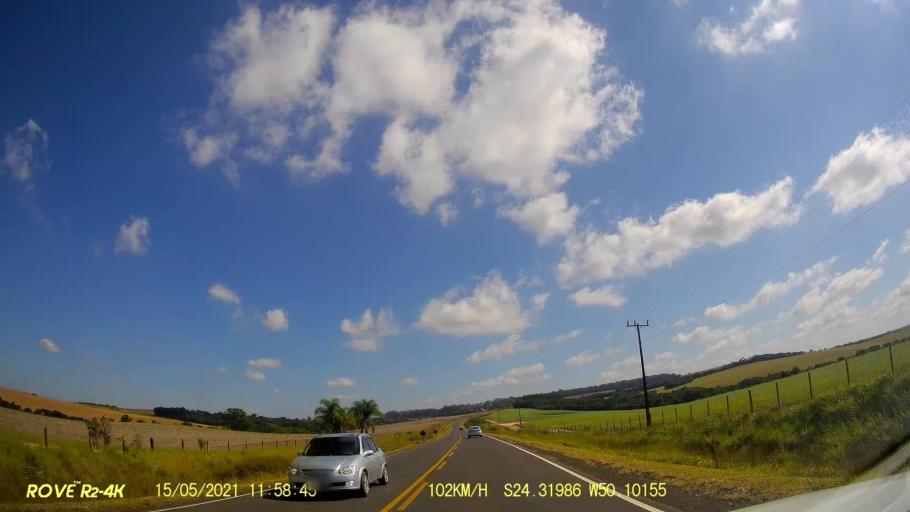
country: BR
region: Parana
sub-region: Pirai Do Sul
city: Pirai do Sul
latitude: -24.3202
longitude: -50.1019
